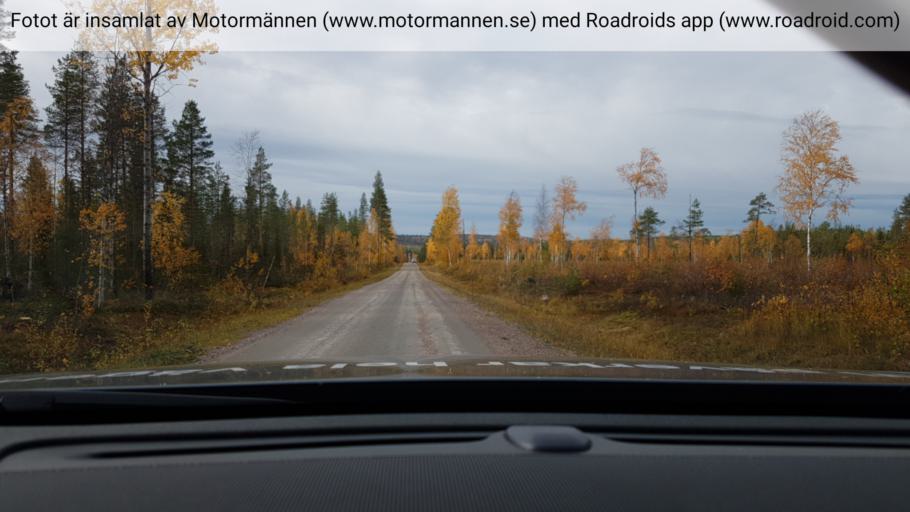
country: SE
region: Norrbotten
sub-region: Overkalix Kommun
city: OEverkalix
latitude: 66.2498
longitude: 23.1851
